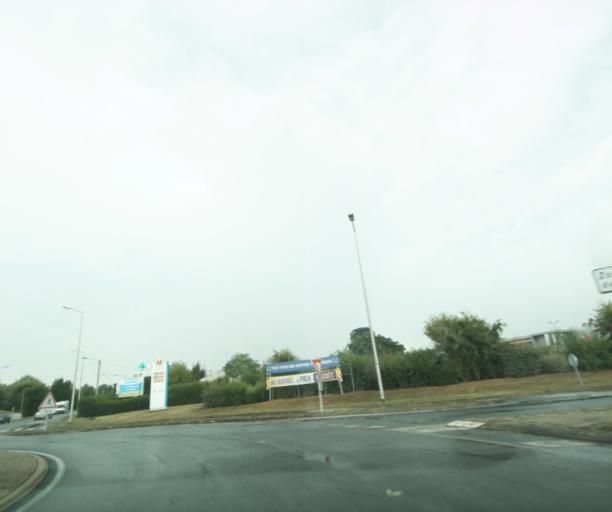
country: FR
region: Poitou-Charentes
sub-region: Departement de la Charente-Maritime
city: Tonnay-Charente
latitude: 45.9506
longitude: -0.8959
